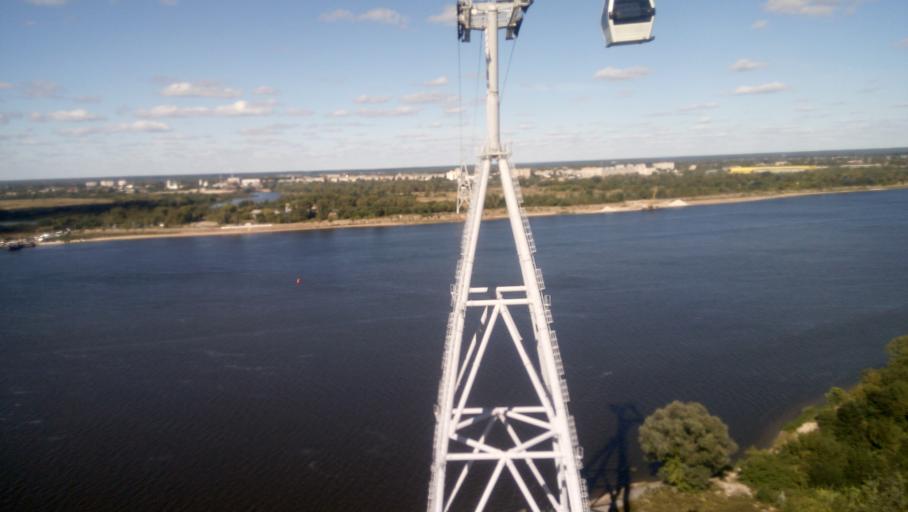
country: RU
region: Nizjnij Novgorod
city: Bor
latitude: 56.3331
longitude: 44.0460
